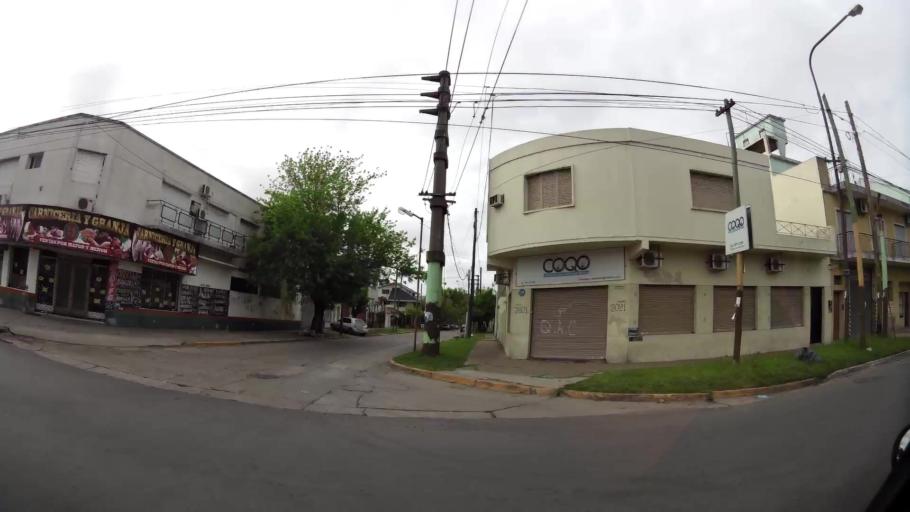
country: AR
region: Buenos Aires
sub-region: Partido de Quilmes
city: Quilmes
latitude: -34.7395
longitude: -58.2742
